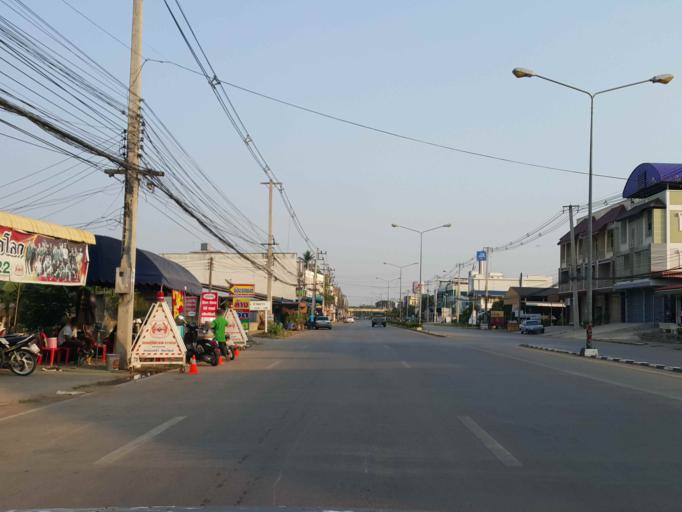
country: TH
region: Sukhothai
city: Sawankhalok
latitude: 17.2995
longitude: 99.8353
